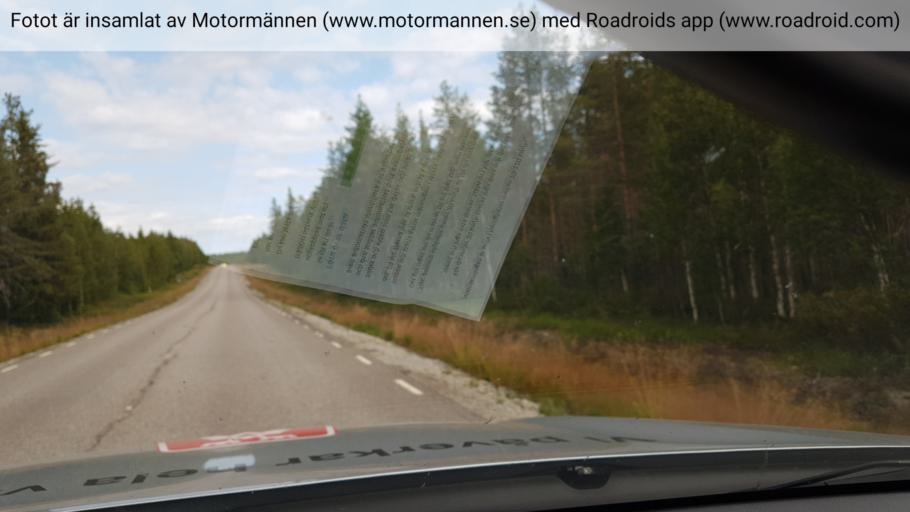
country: SE
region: Vaesterbotten
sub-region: Skelleftea Kommun
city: Boliden
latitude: 65.2314
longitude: 20.2399
